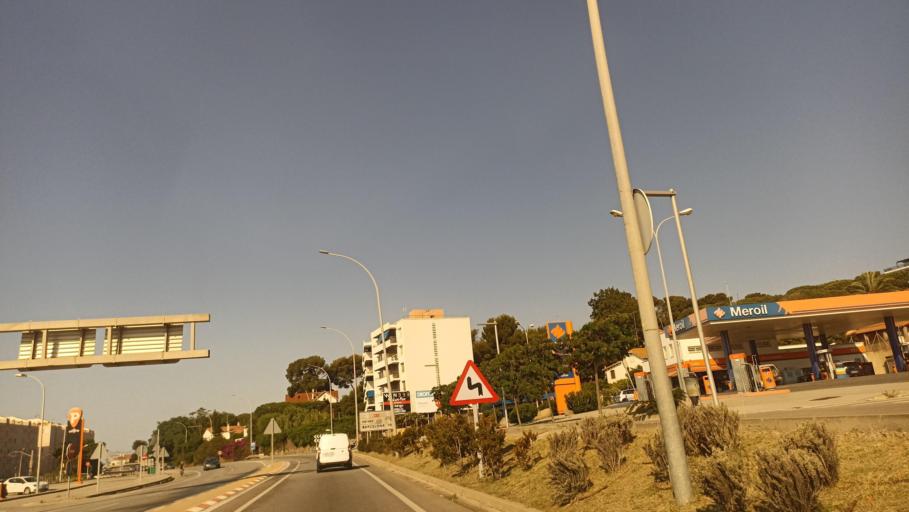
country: ES
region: Catalonia
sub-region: Provincia de Barcelona
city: Sant Andreu de Llavaneres
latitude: 41.5556
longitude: 2.4976
